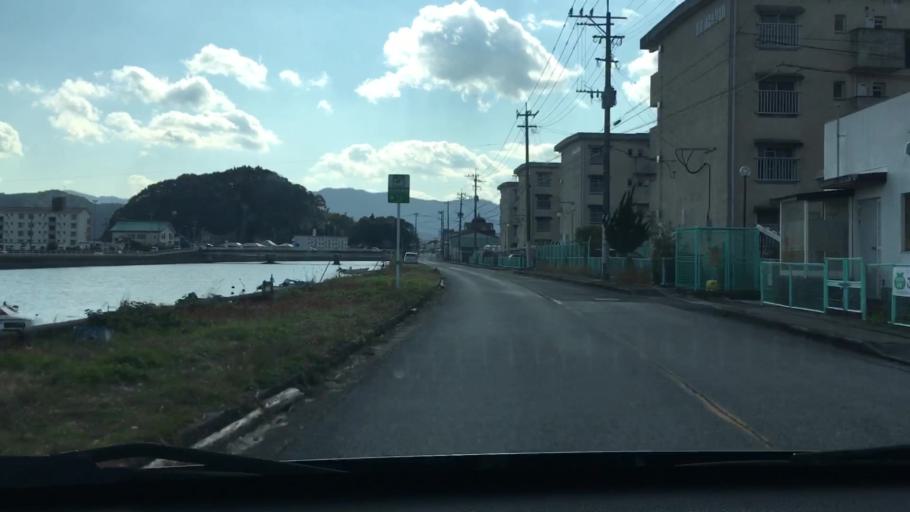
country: JP
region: Oita
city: Saiki
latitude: 32.9644
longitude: 131.9129
